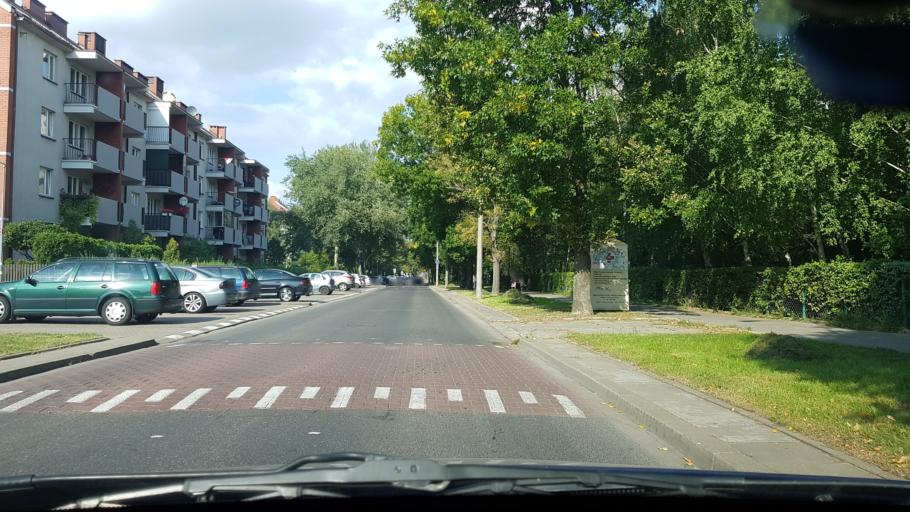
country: PL
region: Masovian Voivodeship
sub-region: Warszawa
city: Bielany
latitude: 52.2797
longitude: 20.9341
